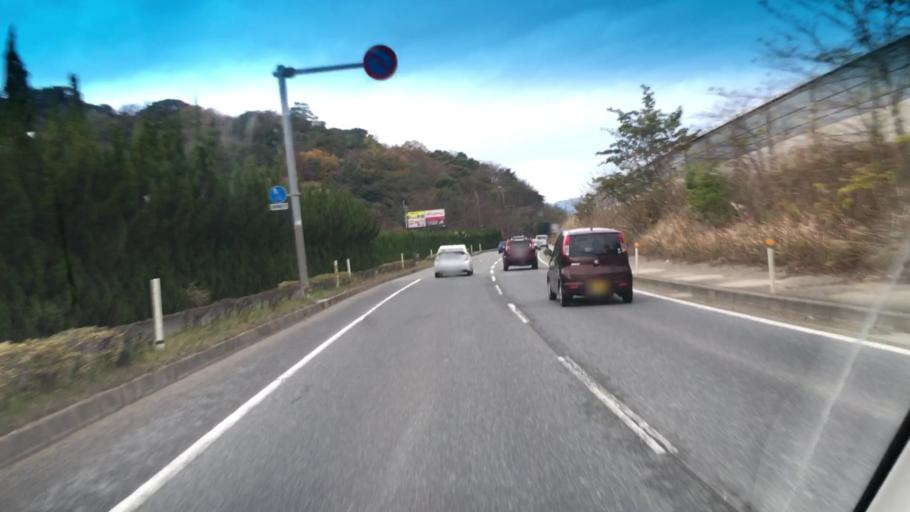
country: JP
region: Fukuoka
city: Maebaru-chuo
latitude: 33.5699
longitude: 130.2902
